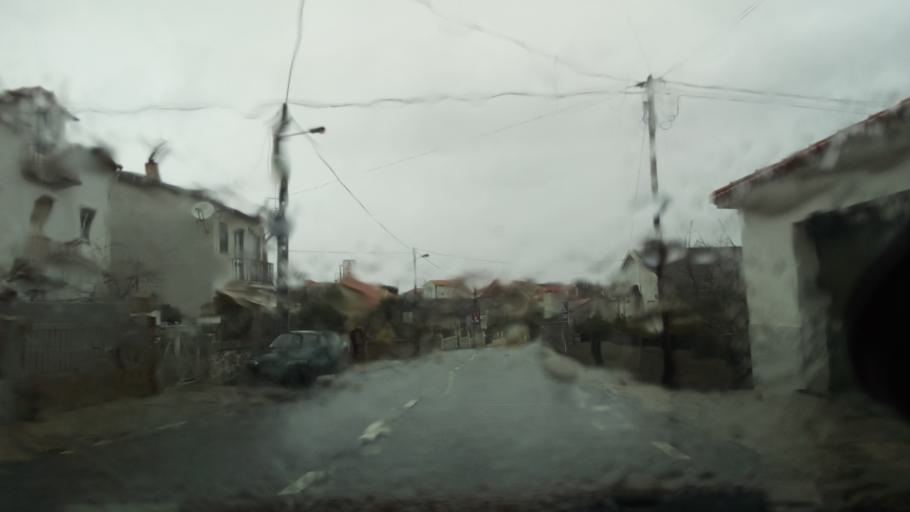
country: PT
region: Guarda
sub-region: Fornos de Algodres
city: Fornos de Algodres
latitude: 40.5217
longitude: -7.5804
